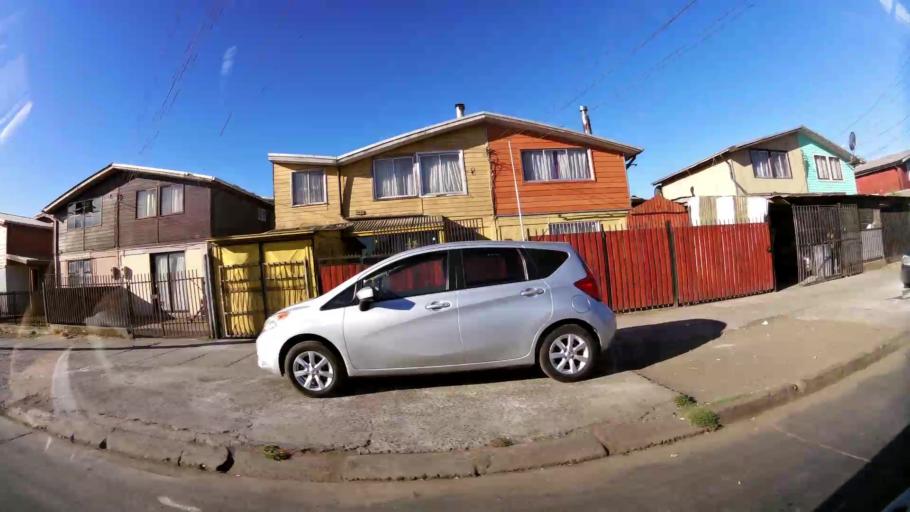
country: CL
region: Biobio
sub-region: Provincia de Concepcion
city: Concepcion
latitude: -36.8290
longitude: -73.1237
